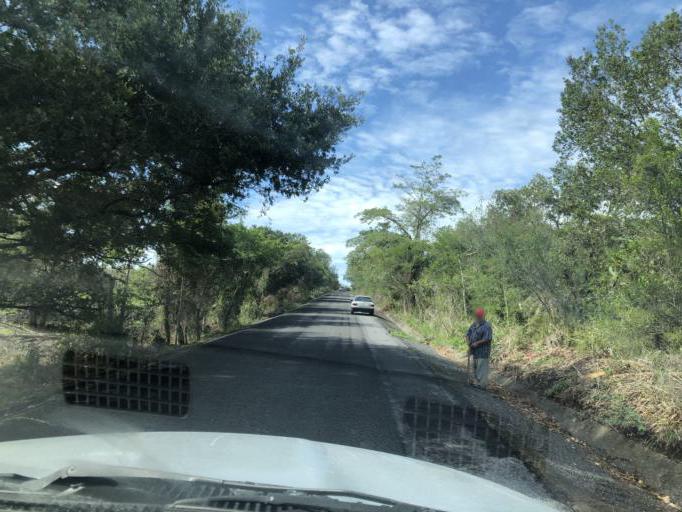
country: MX
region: Veracruz
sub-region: Alto Lucero de Gutierrez Barrios
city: Palma Sola
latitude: 19.7972
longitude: -96.5470
